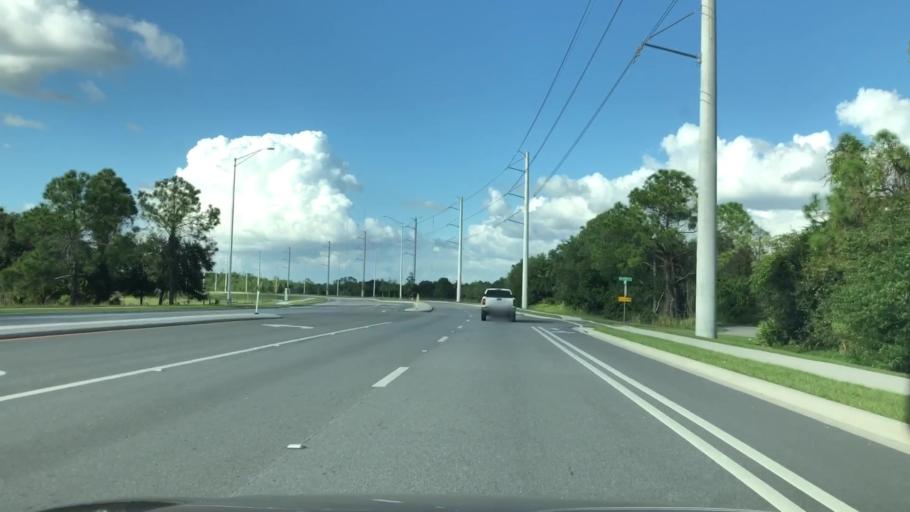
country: US
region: Florida
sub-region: Sarasota County
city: Fruitville
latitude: 27.3473
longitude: -82.3836
